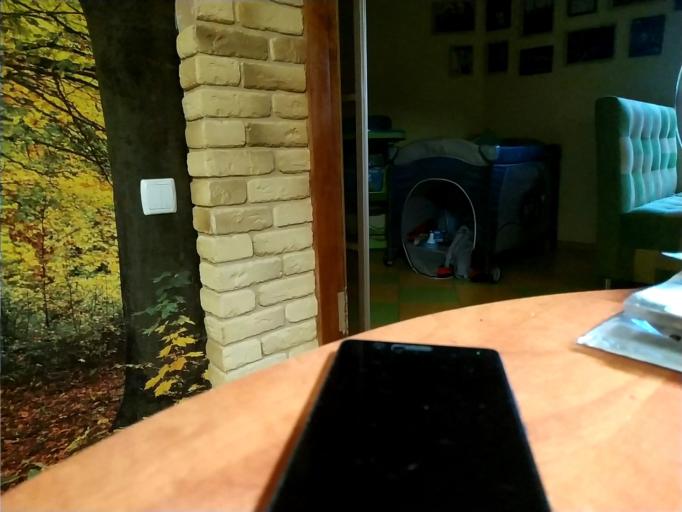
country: RU
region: Orjol
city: Znamenskoye
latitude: 53.4410
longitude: 35.5298
